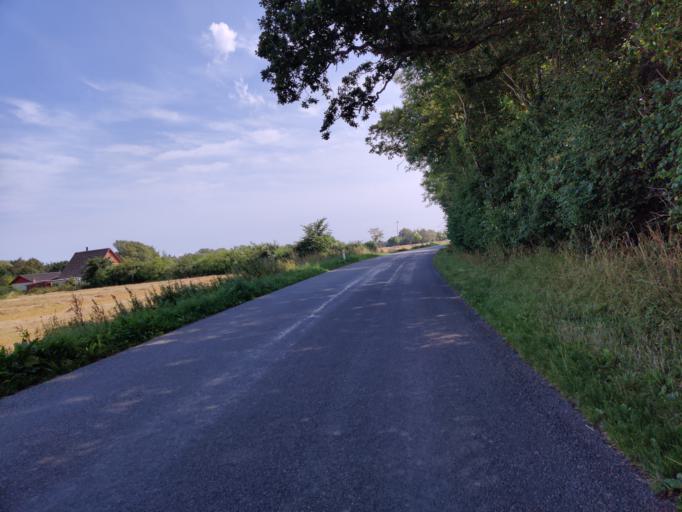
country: DK
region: Zealand
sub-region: Guldborgsund Kommune
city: Nykobing Falster
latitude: 54.6447
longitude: 11.8929
